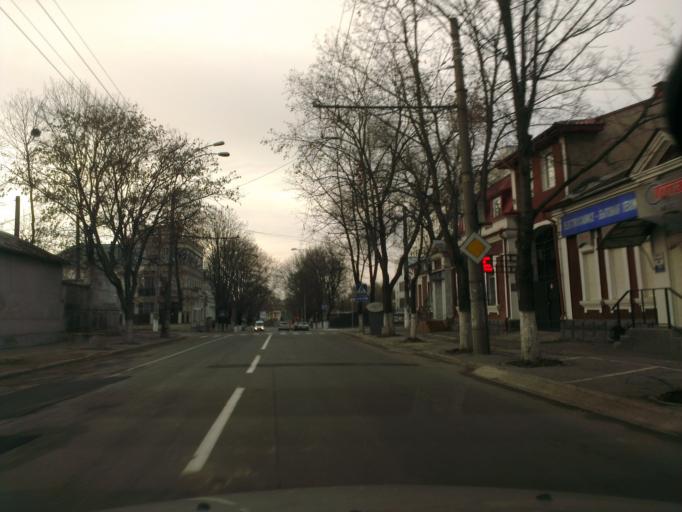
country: MD
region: Chisinau
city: Chisinau
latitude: 47.0274
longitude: 28.8194
